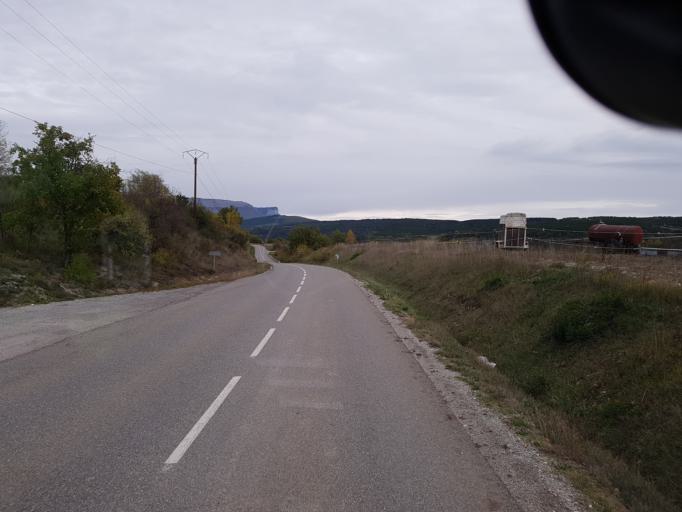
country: FR
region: Provence-Alpes-Cote d'Azur
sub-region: Departement des Hautes-Alpes
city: Laragne-Monteglin
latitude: 44.3228
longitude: 5.7386
